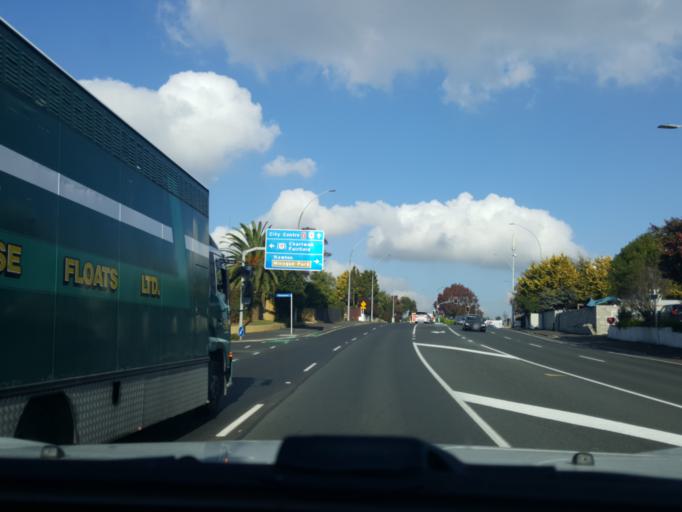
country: NZ
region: Waikato
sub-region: Hamilton City
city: Hamilton
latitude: -37.7681
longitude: 175.2615
